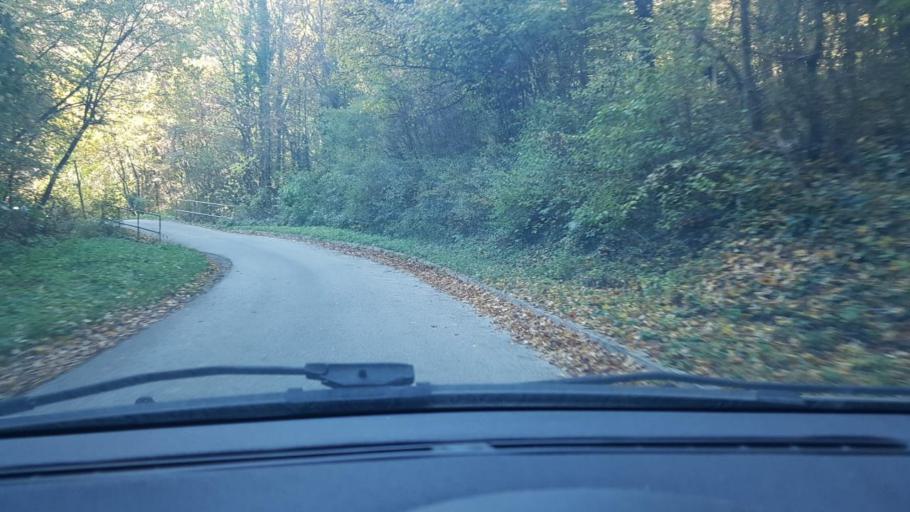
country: HR
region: Krapinsko-Zagorska
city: Zlatar
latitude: 46.1555
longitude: 16.0724
